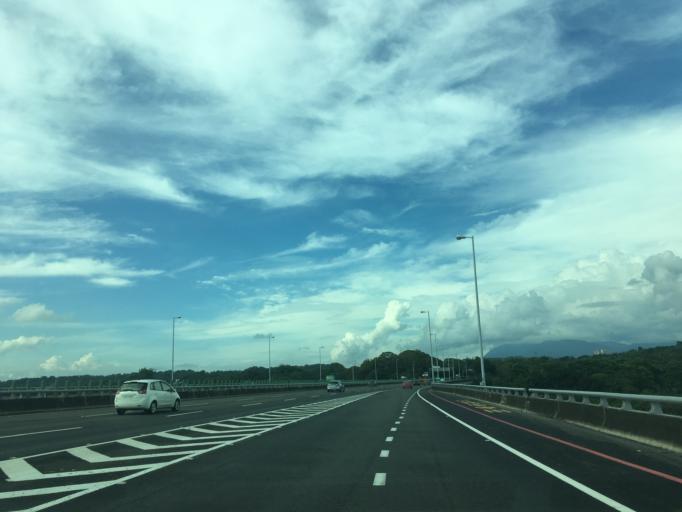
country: TW
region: Taiwan
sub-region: Chiayi
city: Jiayi Shi
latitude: 23.4538
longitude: 120.4870
